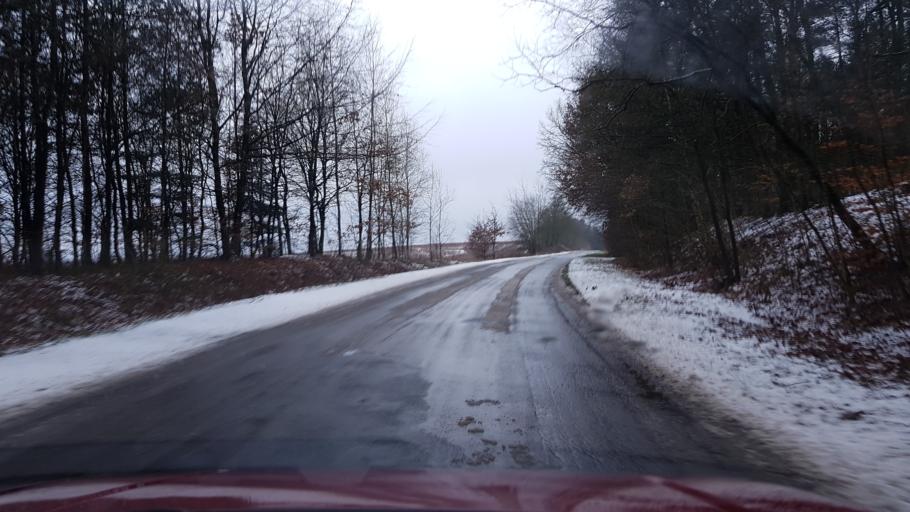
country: PL
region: West Pomeranian Voivodeship
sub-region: Powiat goleniowski
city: Nowogard
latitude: 53.6320
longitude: 15.1229
